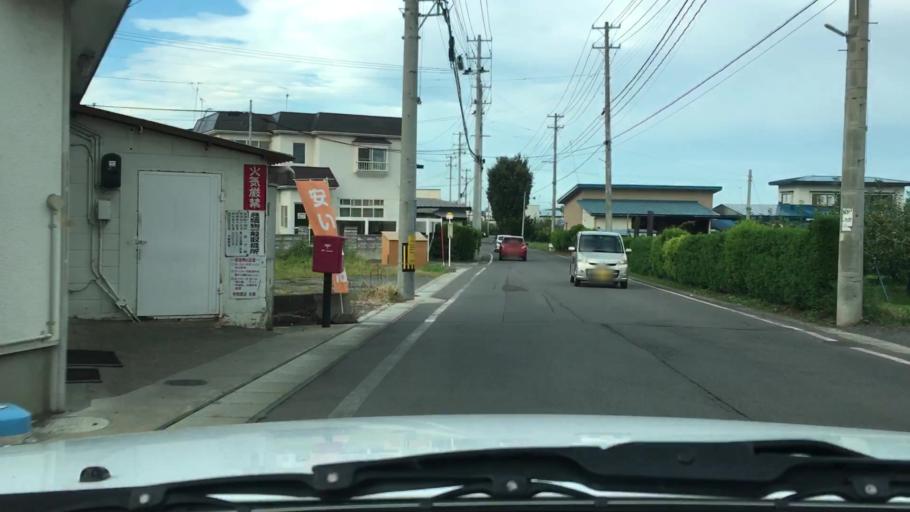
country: JP
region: Aomori
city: Hirosaki
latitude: 40.5841
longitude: 140.4602
